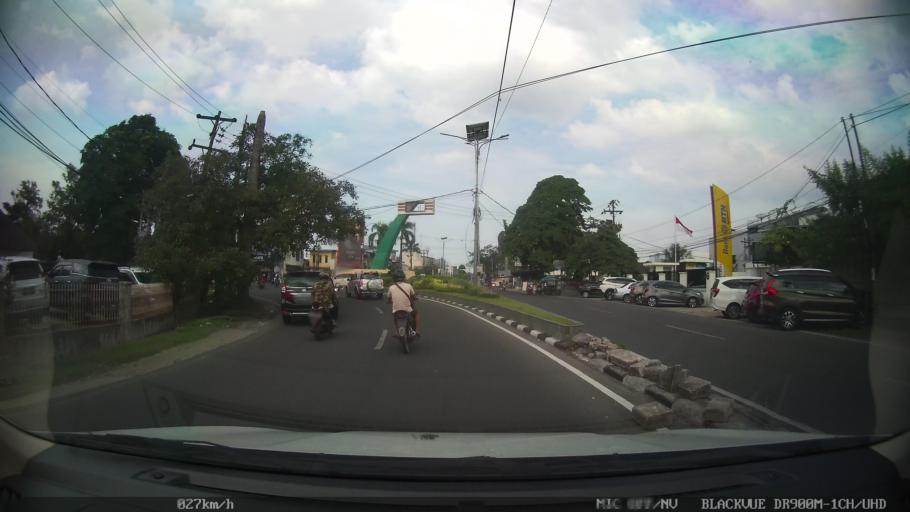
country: ID
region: North Sumatra
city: Medan
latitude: 3.5722
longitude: 98.6809
